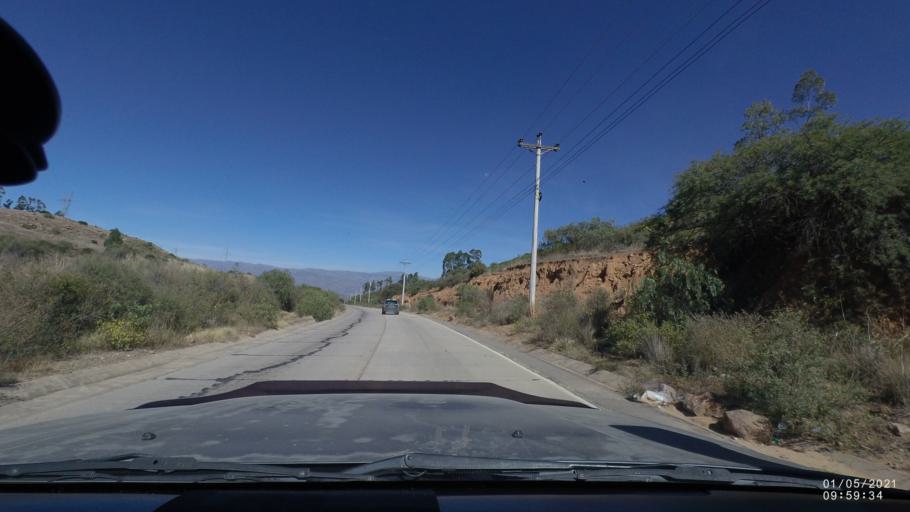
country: BO
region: Cochabamba
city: Cochabamba
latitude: -17.5264
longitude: -66.1900
